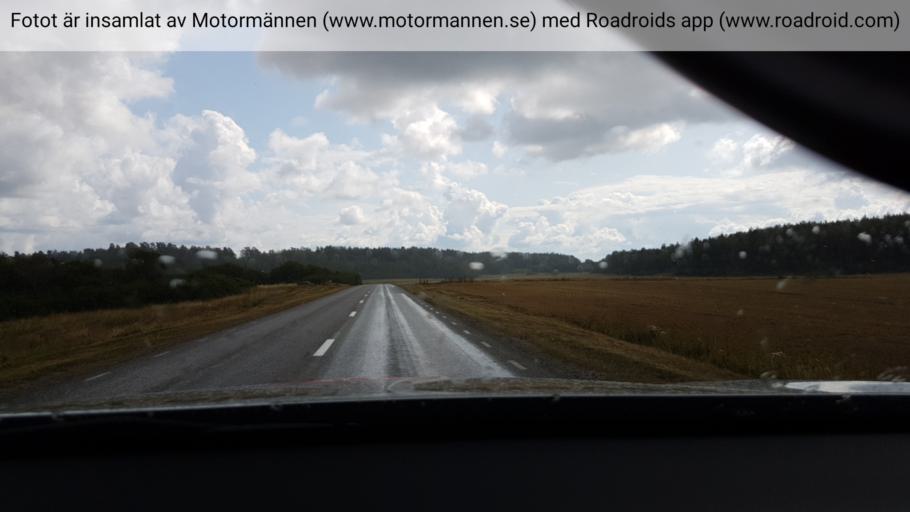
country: SE
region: Stockholm
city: Stenhamra
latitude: 59.3958
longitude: 17.5694
